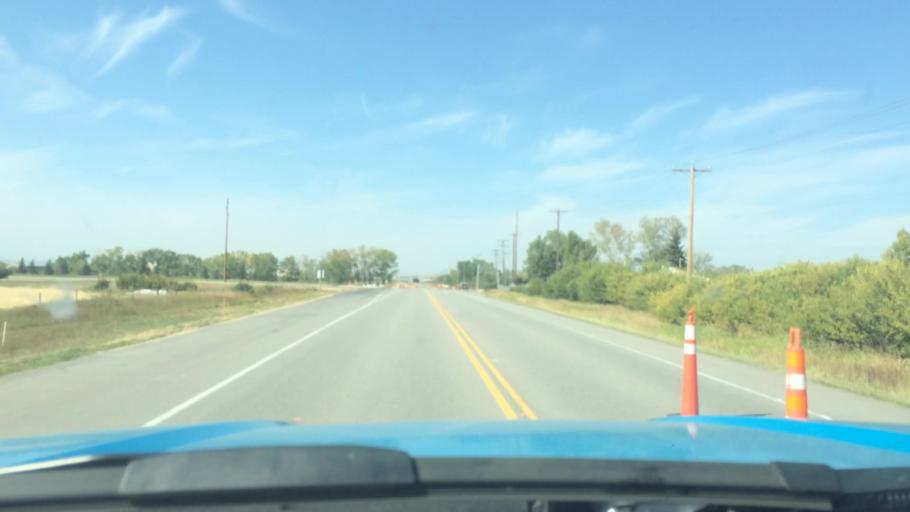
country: CA
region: Alberta
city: Airdrie
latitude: 51.2126
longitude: -113.9553
